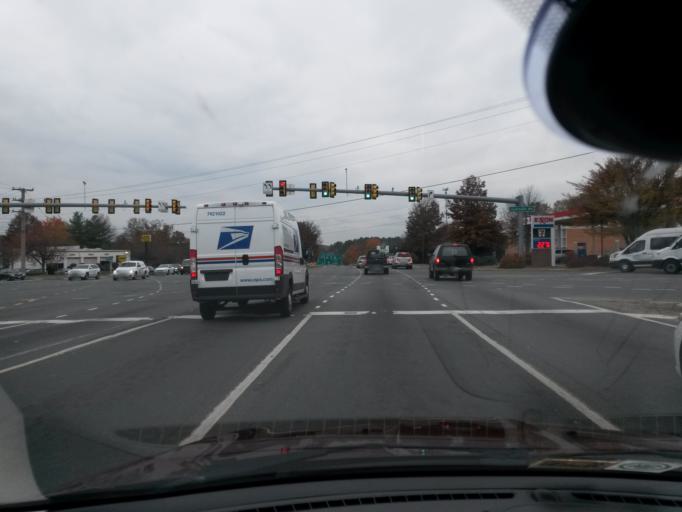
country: US
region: Virginia
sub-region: City of Charlottesville
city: Charlottesville
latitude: 38.0624
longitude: -78.4914
